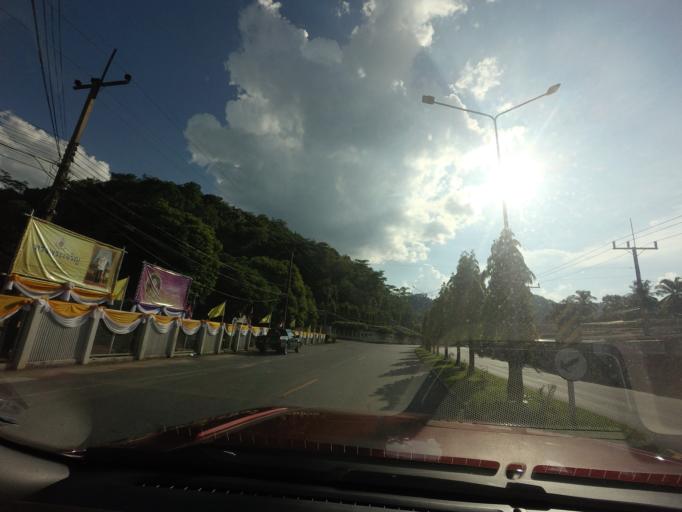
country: TH
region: Yala
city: Than To
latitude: 6.1608
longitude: 101.2736
